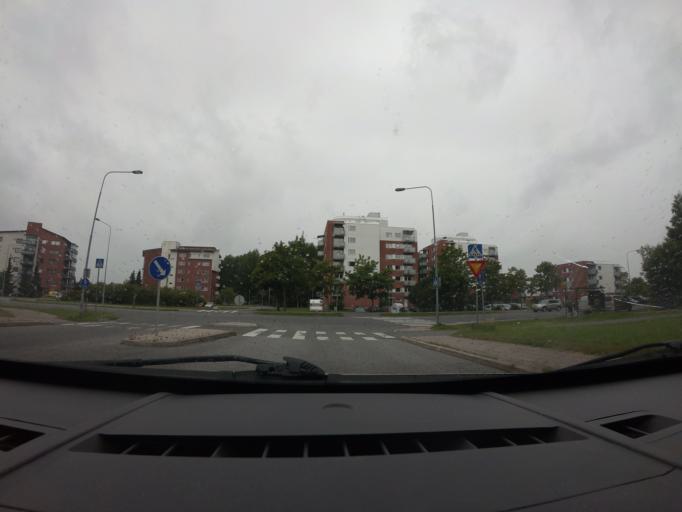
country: FI
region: Varsinais-Suomi
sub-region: Turku
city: Turku
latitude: 60.4189
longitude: 22.3022
